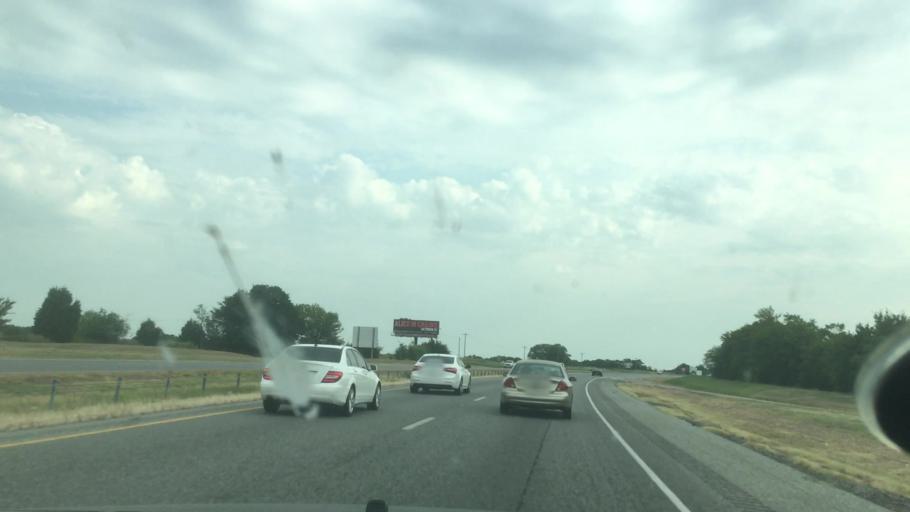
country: US
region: Oklahoma
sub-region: Bryan County
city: Colbert
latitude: 33.8645
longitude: -96.5113
